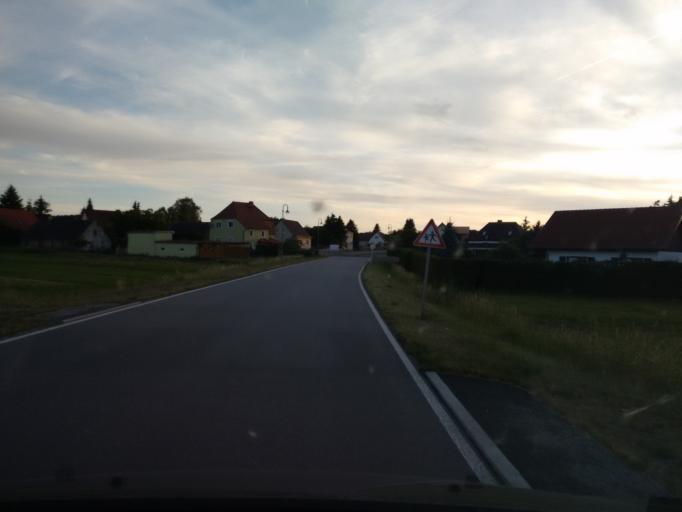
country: DE
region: Brandenburg
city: Gross Lindow
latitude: 52.1386
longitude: 14.4883
